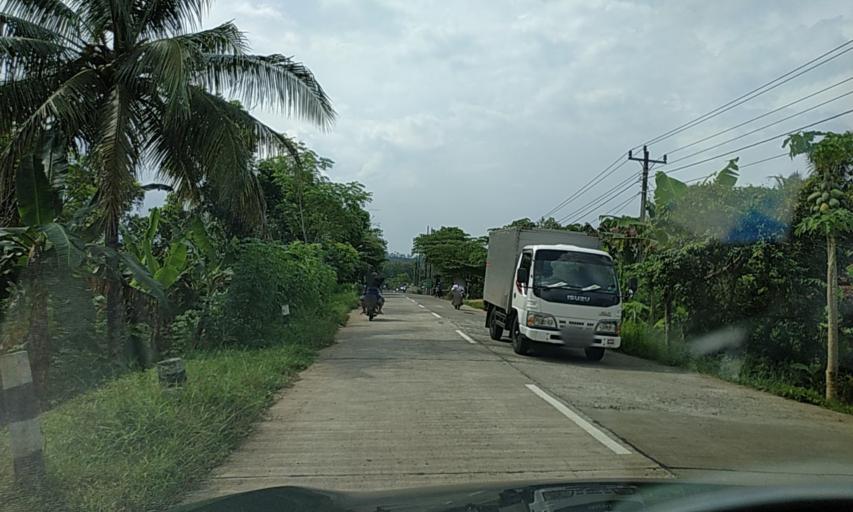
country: ID
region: Central Java
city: Winangun
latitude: -7.3551
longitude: 108.7063
